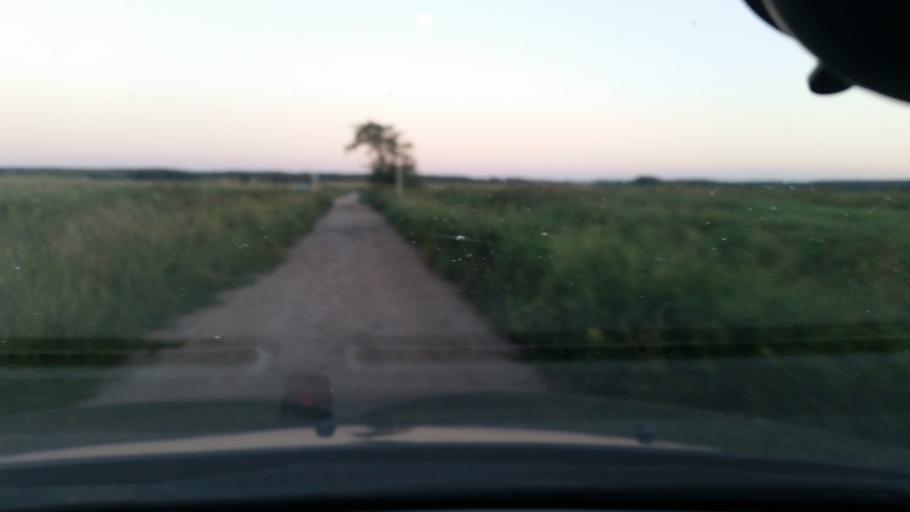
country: PL
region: Pomeranian Voivodeship
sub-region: Powiat wejherowski
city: Choczewo
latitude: 54.7898
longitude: 17.7931
